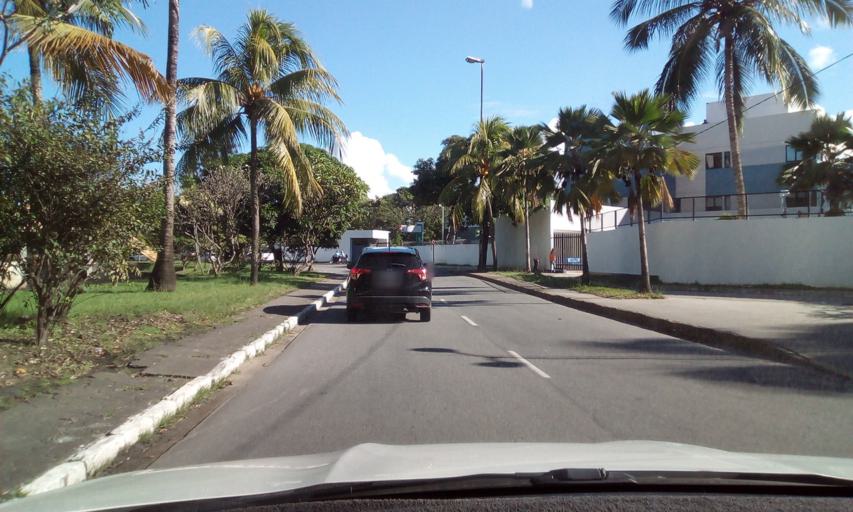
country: BR
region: Pernambuco
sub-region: Recife
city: Recife
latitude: -8.0656
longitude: -34.8978
